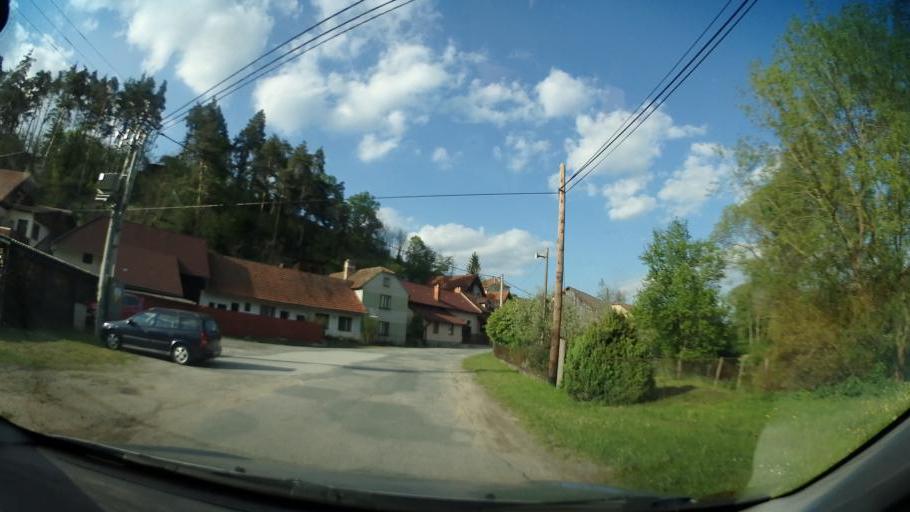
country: CZ
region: Vysocina
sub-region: Okres Zd'ar nad Sazavou
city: Velke Mezirici
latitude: 49.3348
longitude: 15.9547
